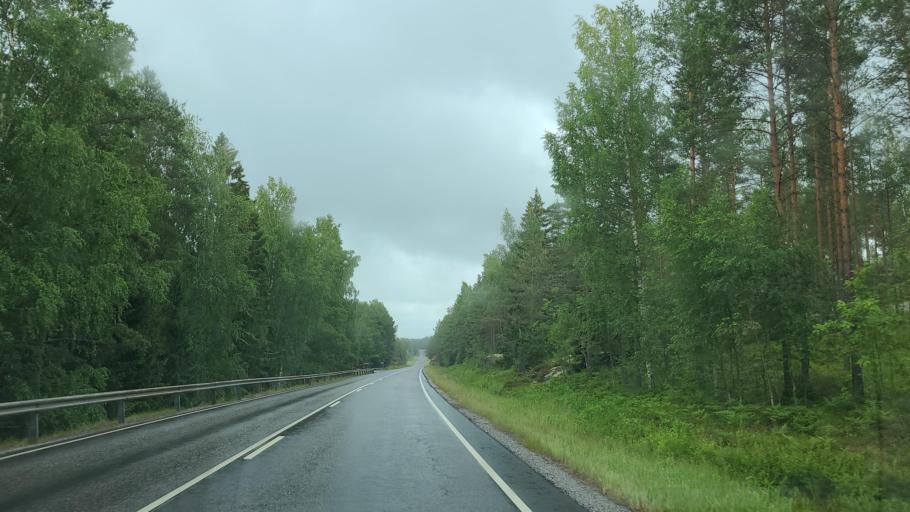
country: FI
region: Varsinais-Suomi
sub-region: Aboland-Turunmaa
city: Kimito
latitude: 60.2211
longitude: 22.6324
